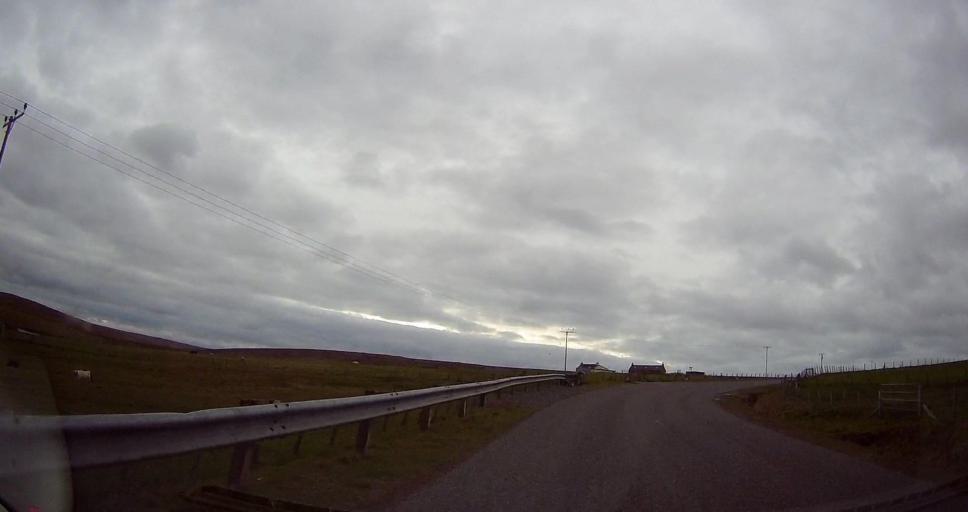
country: GB
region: Scotland
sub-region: Shetland Islands
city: Shetland
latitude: 60.6613
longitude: -1.0485
